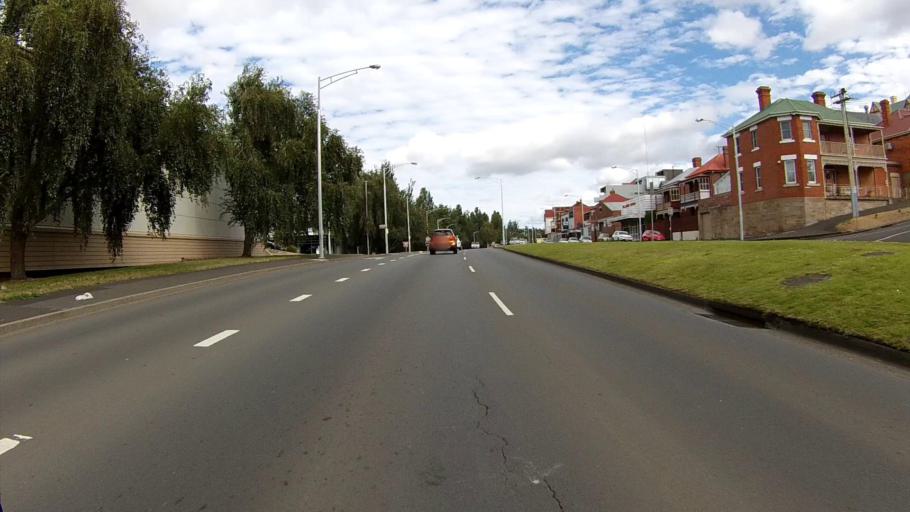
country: AU
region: Tasmania
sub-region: Hobart
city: Hobart
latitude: -42.8769
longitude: 147.3284
